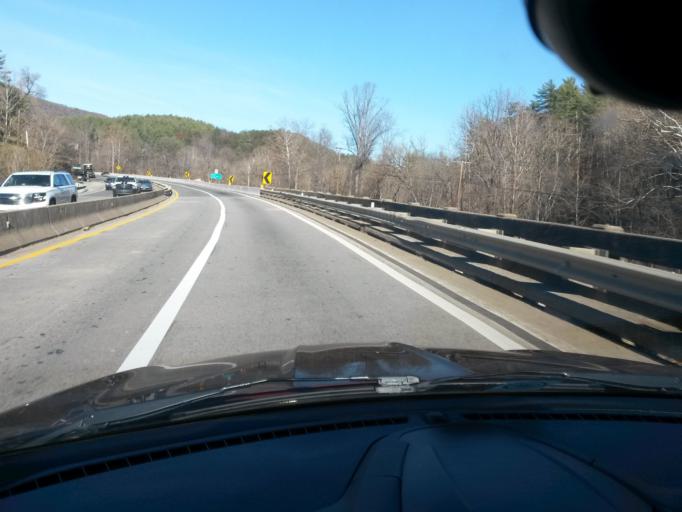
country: US
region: Virginia
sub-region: Roanoke County
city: Narrows
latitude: 37.1790
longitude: -79.9354
